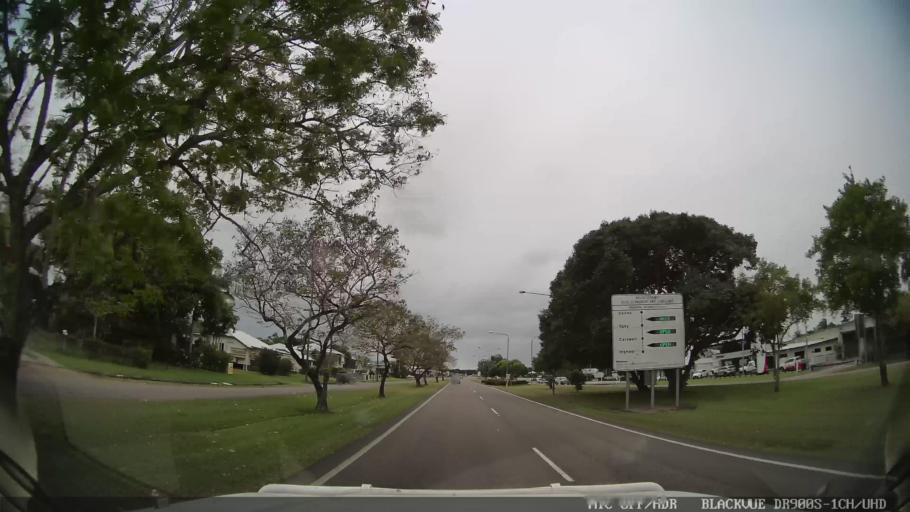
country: AU
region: Queensland
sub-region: Hinchinbrook
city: Ingham
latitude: -18.6451
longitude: 146.1623
